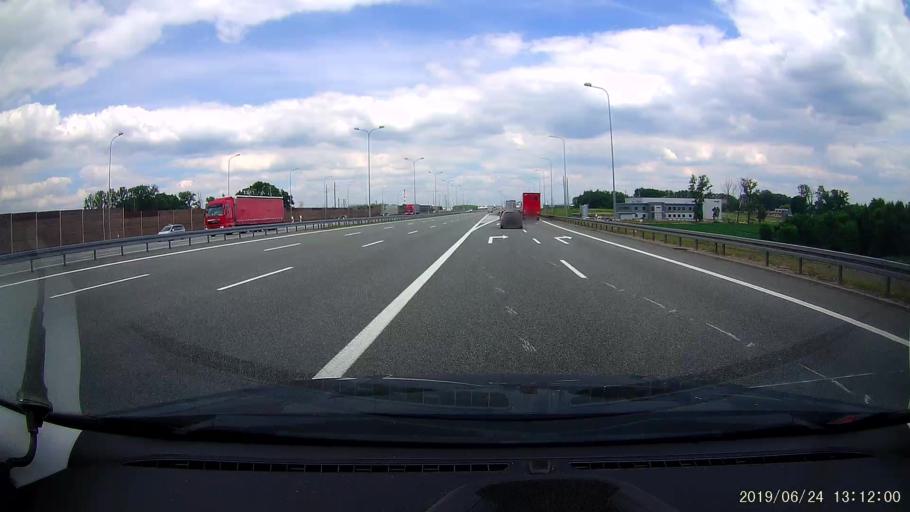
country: PL
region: Silesian Voivodeship
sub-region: Powiat gliwicki
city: Przyszowice
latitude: 50.2524
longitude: 18.7163
